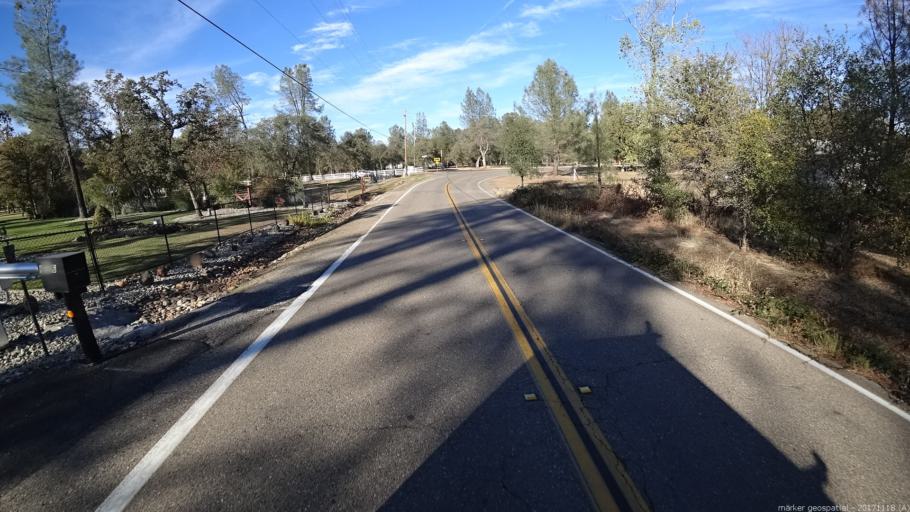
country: US
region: California
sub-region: Shasta County
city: Redding
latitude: 40.4844
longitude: -122.4550
